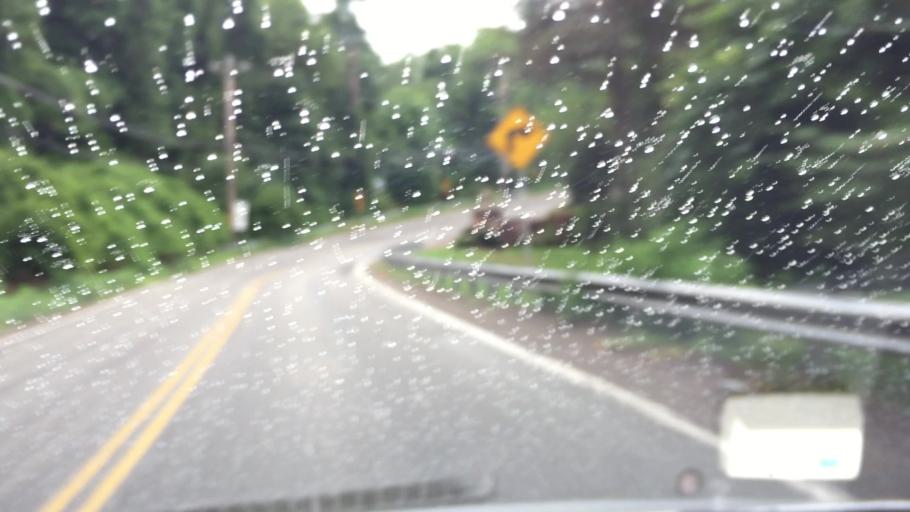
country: US
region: Pennsylvania
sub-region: Allegheny County
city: Carnegie
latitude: 40.4318
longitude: -80.0947
